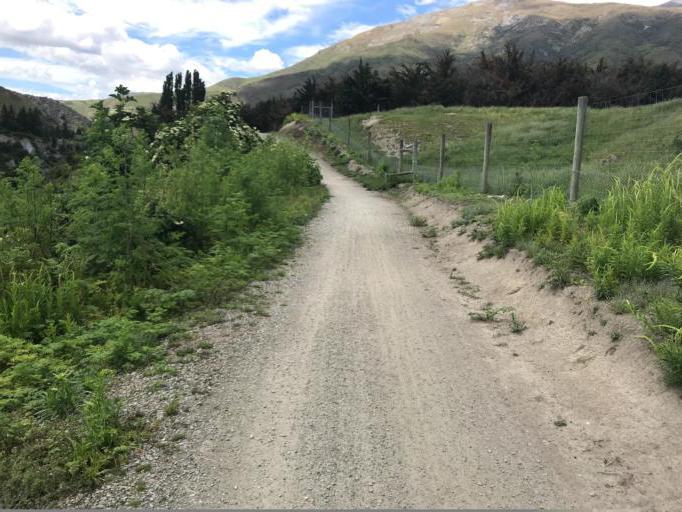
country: NZ
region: Otago
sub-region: Queenstown-Lakes District
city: Arrowtown
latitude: -44.9986
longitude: 168.8689
